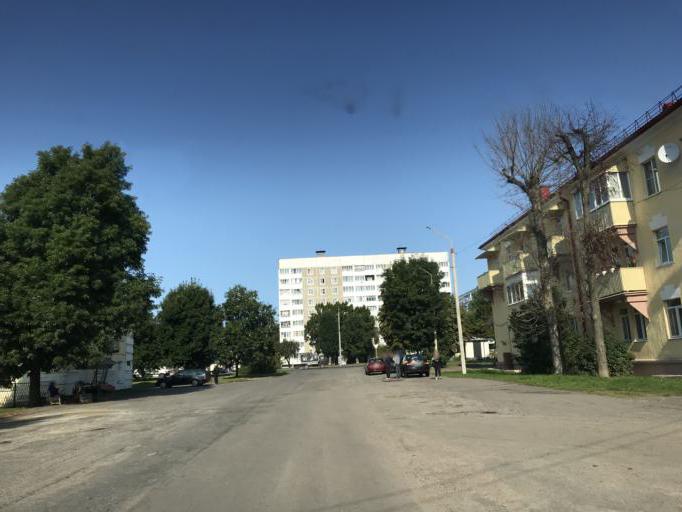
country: BY
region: Mogilev
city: Buynichy
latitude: 53.8816
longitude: 30.2705
